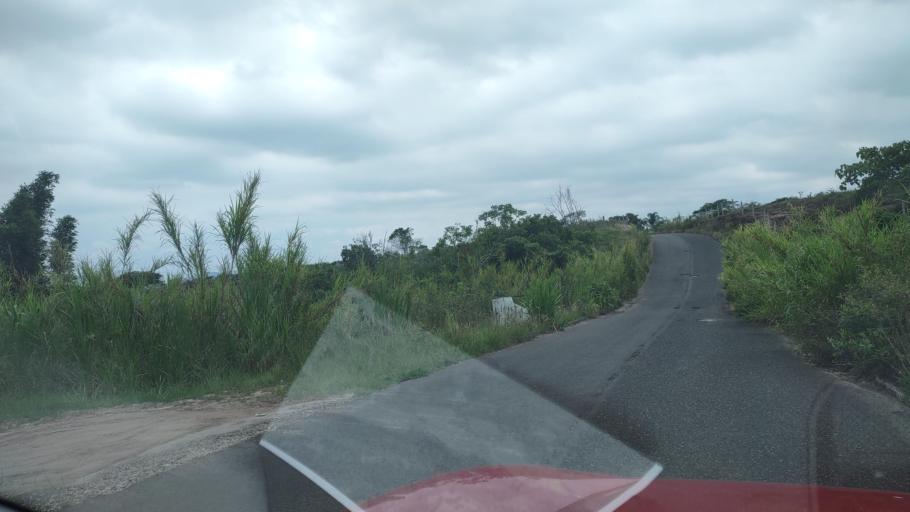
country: MX
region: Veracruz
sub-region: Emiliano Zapata
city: Dos Rios
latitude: 19.4840
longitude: -96.8270
